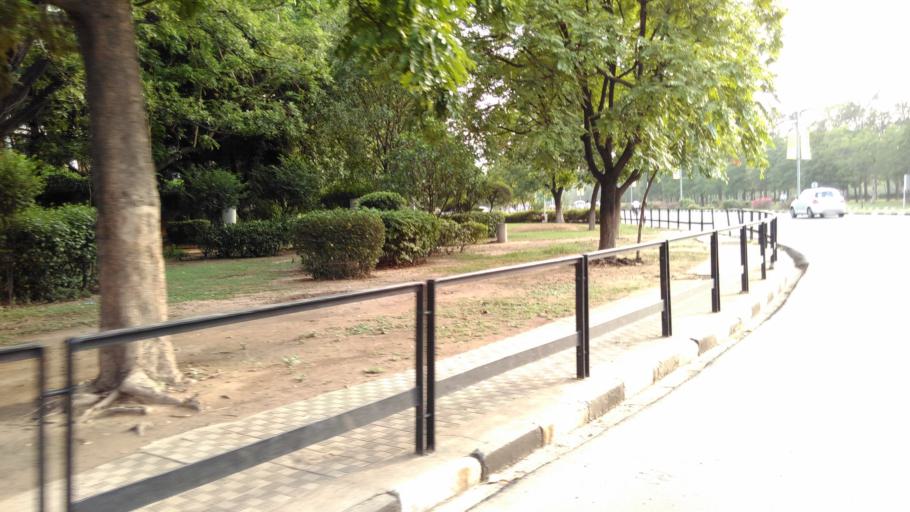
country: IN
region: Chandigarh
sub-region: Chandigarh
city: Chandigarh
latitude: 30.7462
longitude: 76.7853
